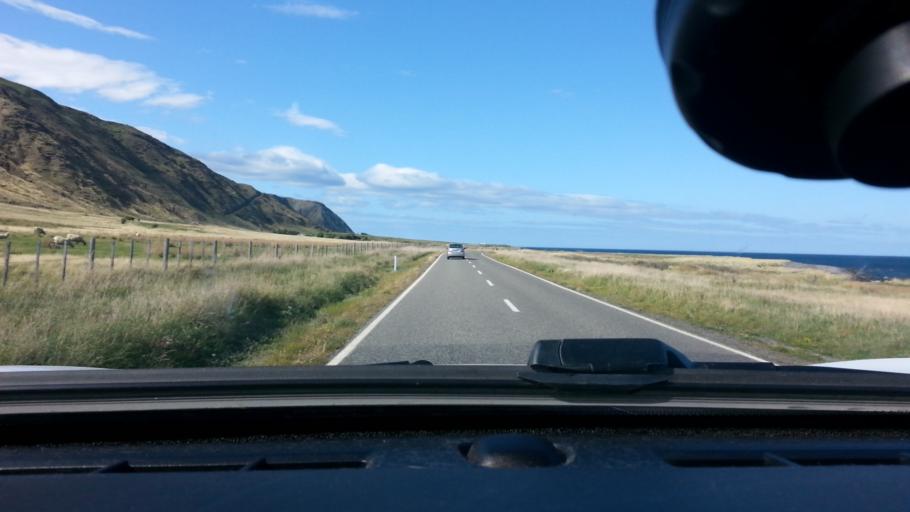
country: NZ
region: Wellington
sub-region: South Wairarapa District
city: Waipawa
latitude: -41.5662
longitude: 175.2234
